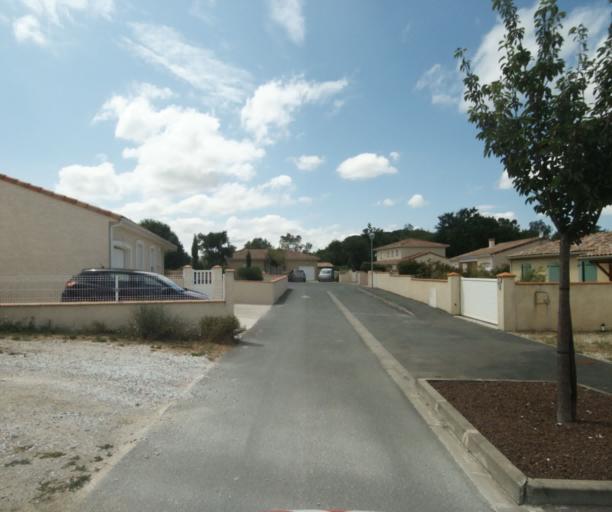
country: FR
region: Midi-Pyrenees
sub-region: Departement de la Haute-Garonne
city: Revel
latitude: 43.4515
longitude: 1.9885
